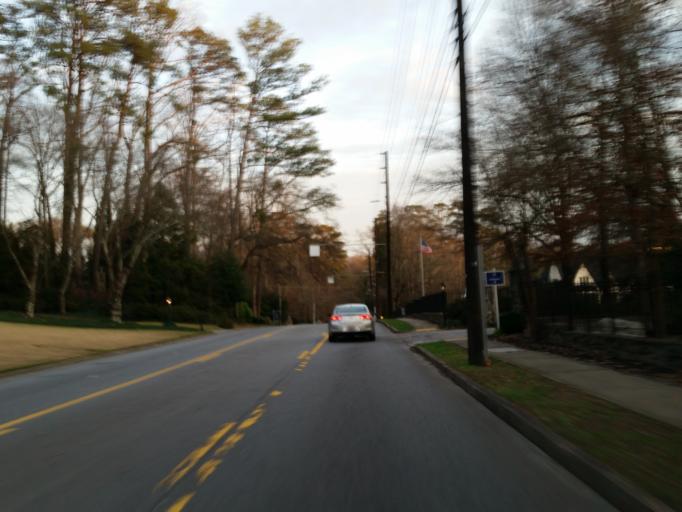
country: US
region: Georgia
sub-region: Cobb County
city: Vinings
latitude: 33.8504
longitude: -84.4175
